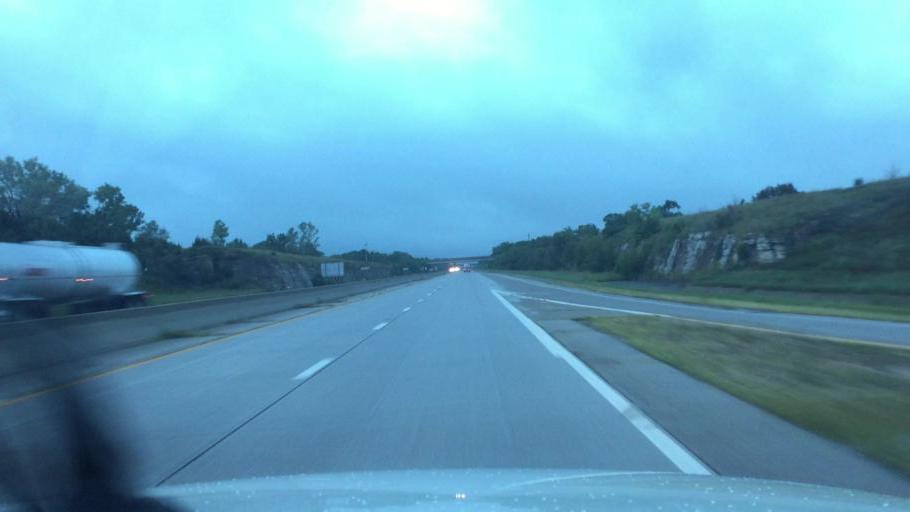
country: US
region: Kansas
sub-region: Neosho County
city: Chanute
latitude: 37.6868
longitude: -95.4796
